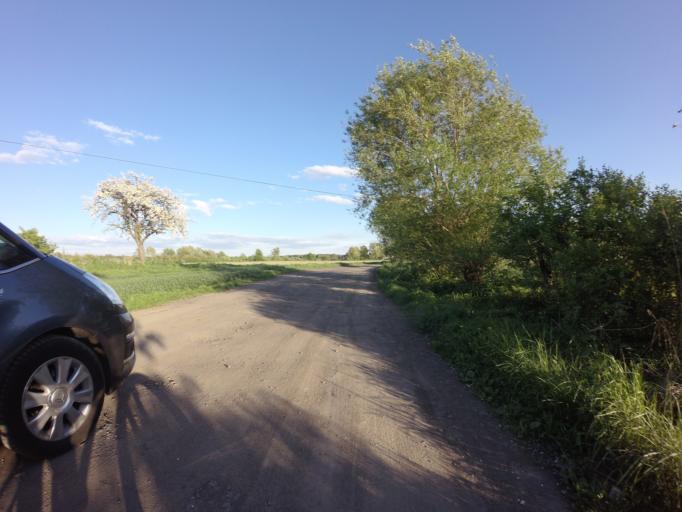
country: PL
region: West Pomeranian Voivodeship
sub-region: Powiat choszczenski
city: Choszczno
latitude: 53.1359
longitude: 15.4391
